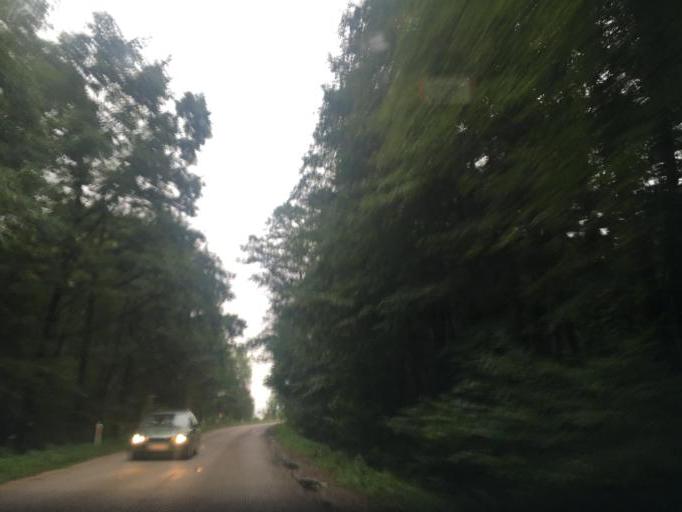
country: PL
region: Podlasie
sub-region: Powiat bielski
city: Bransk
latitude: 52.7319
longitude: 22.7967
